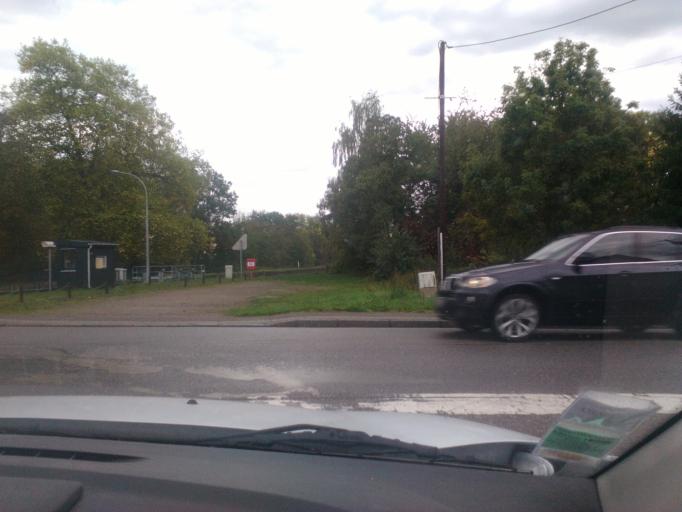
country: FR
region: Lorraine
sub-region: Departement des Vosges
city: Nomexy
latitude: 48.3099
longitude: 6.3873
